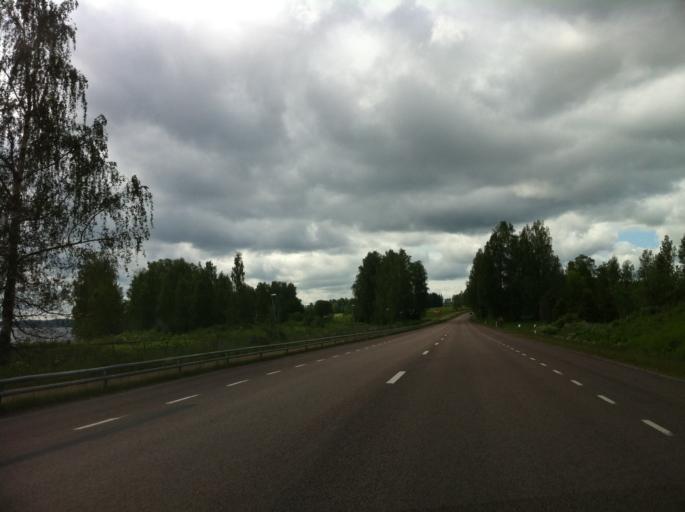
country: SE
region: Vaermland
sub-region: Sunne Kommun
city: Sunne
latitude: 59.8220
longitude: 13.1314
